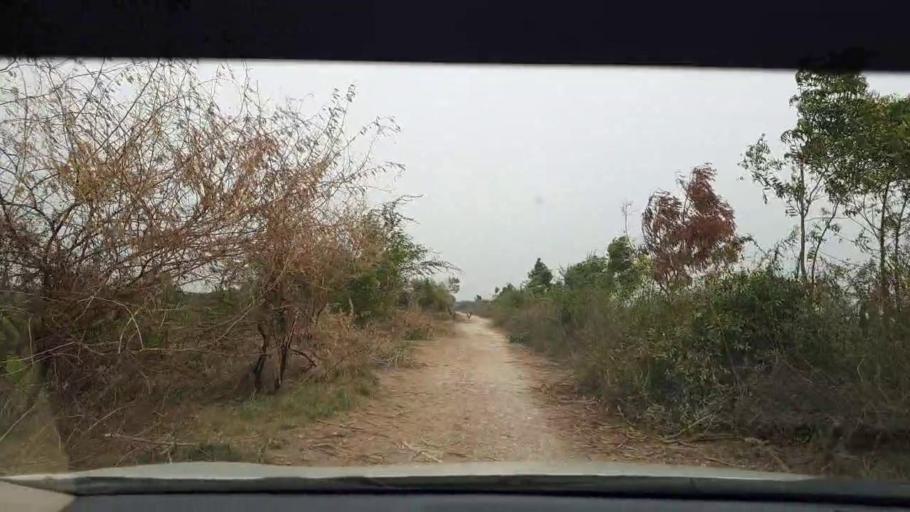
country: PK
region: Sindh
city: Berani
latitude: 25.8946
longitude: 68.7680
